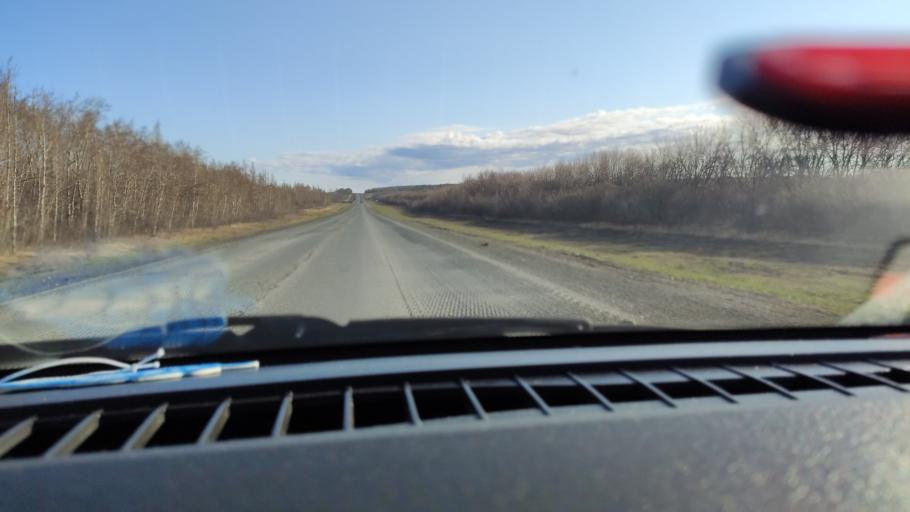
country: RU
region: Saratov
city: Dukhovnitskoye
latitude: 52.6976
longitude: 48.2511
